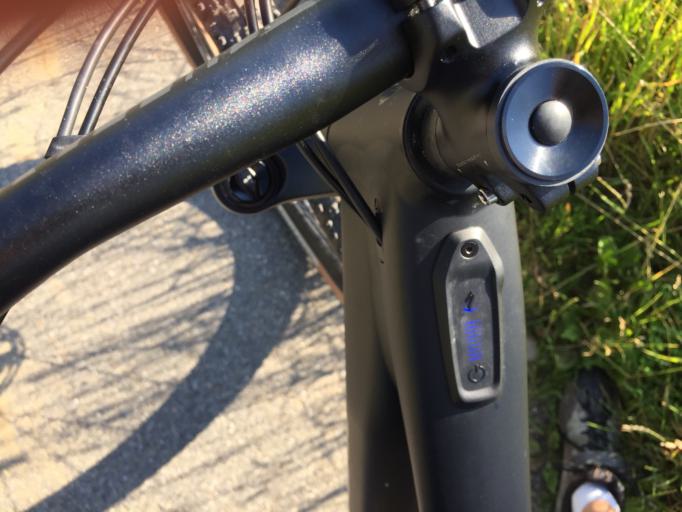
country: CH
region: Bern
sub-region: Bern-Mittelland District
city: Niederwichtrach
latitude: 46.8243
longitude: 7.5888
